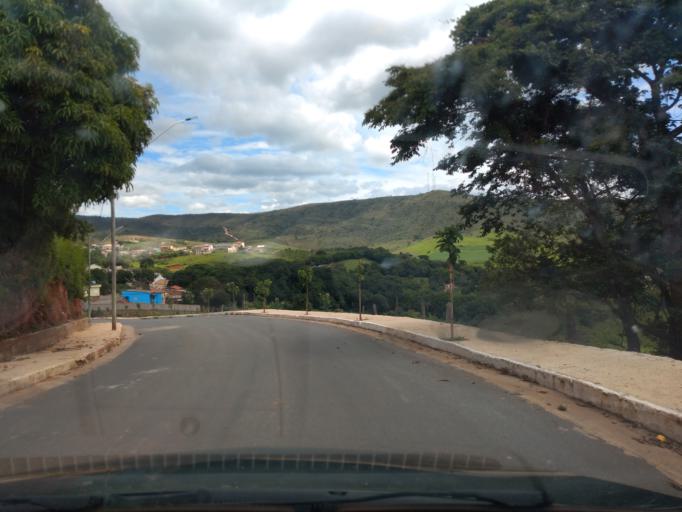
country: BR
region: Minas Gerais
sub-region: Lavras
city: Lavras
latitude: -21.5107
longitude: -44.9091
